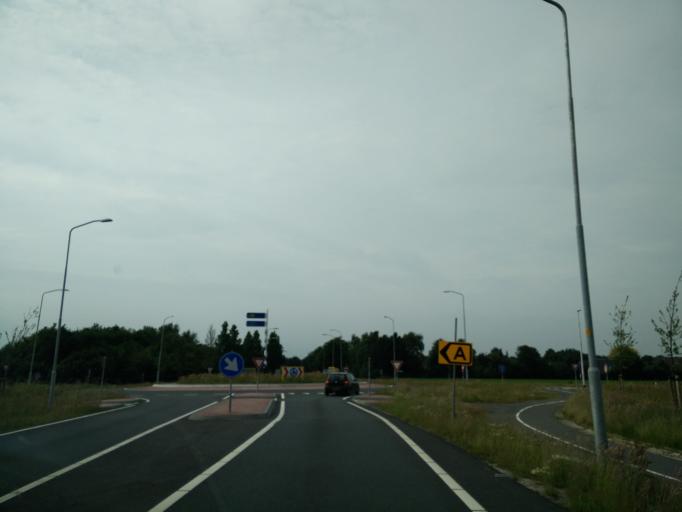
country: NL
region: Drenthe
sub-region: Gemeente Aa en Hunze
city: Anloo
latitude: 52.9757
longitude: 6.6519
